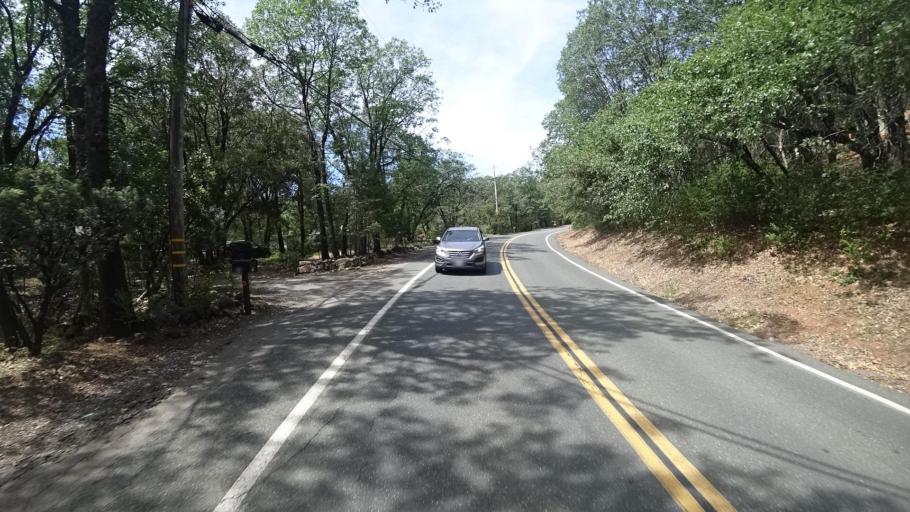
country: US
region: California
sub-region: Lake County
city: Cobb
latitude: 38.8656
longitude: -122.6885
